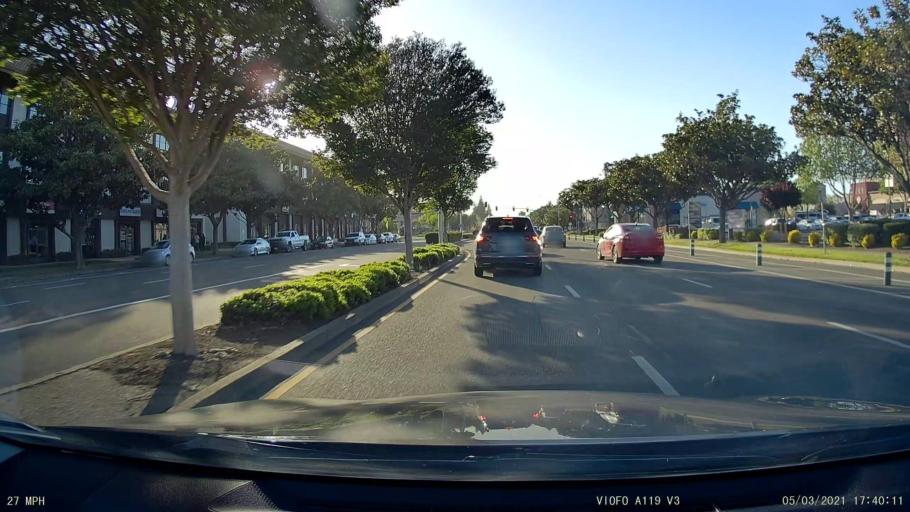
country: US
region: California
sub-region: Alameda County
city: Fremont
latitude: 37.5541
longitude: -121.9784
